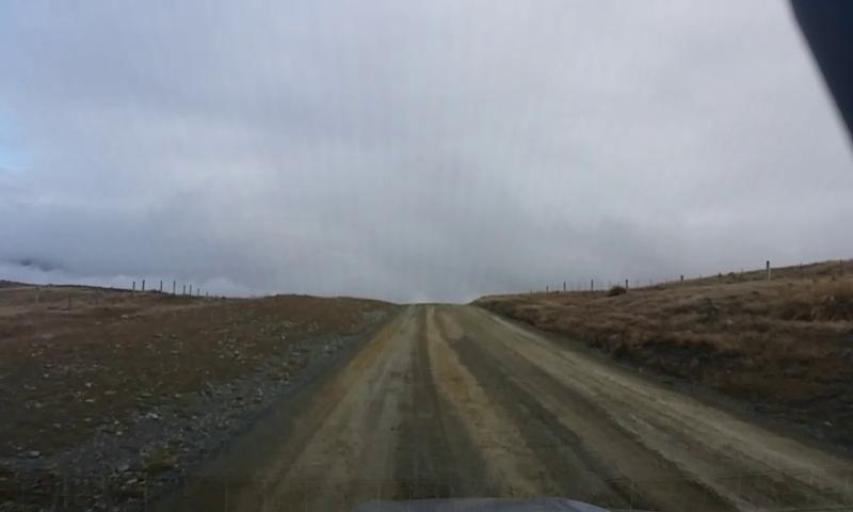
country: NZ
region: Canterbury
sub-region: Ashburton District
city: Methven
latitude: -43.6151
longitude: 171.1605
